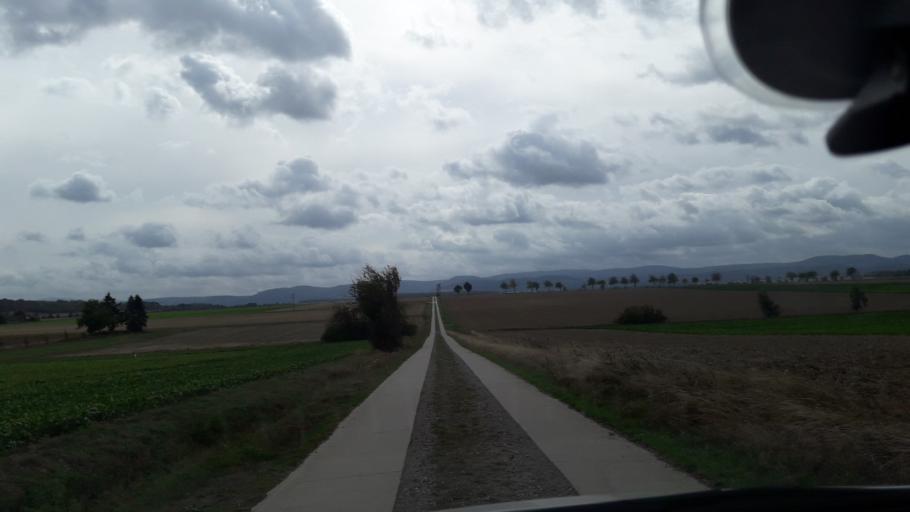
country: DE
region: Lower Saxony
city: Liebenburg
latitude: 51.9989
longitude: 10.3907
